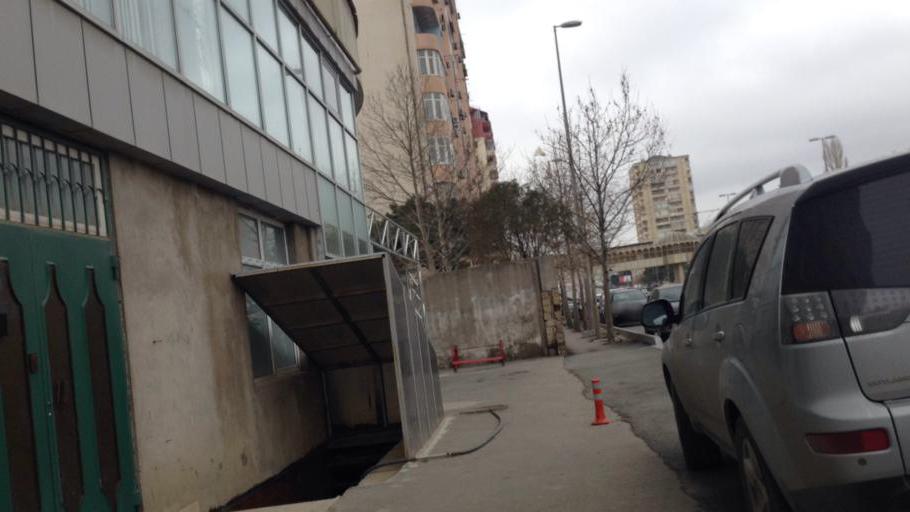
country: AZ
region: Baki
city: Bilajari
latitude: 40.4122
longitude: 49.8426
